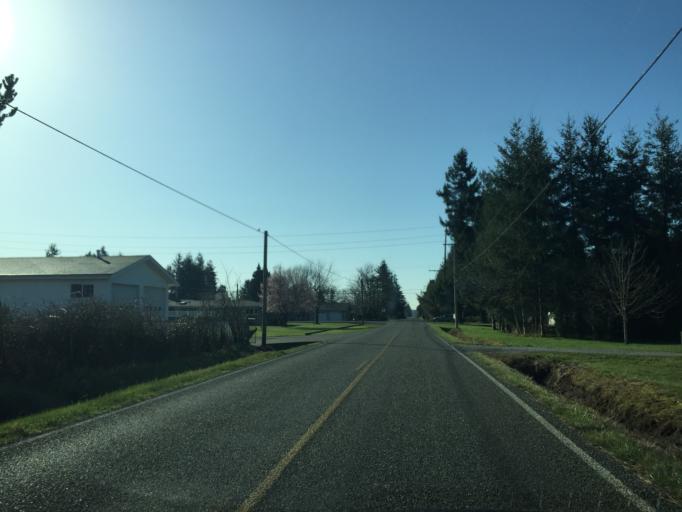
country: US
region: Washington
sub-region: Whatcom County
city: Lynden
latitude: 48.8781
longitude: -122.4969
